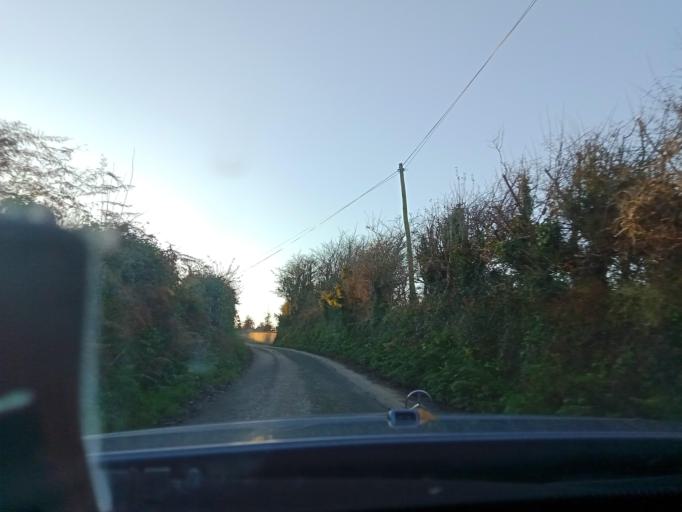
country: IE
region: Leinster
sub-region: Loch Garman
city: New Ross
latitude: 52.3726
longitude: -7.0221
